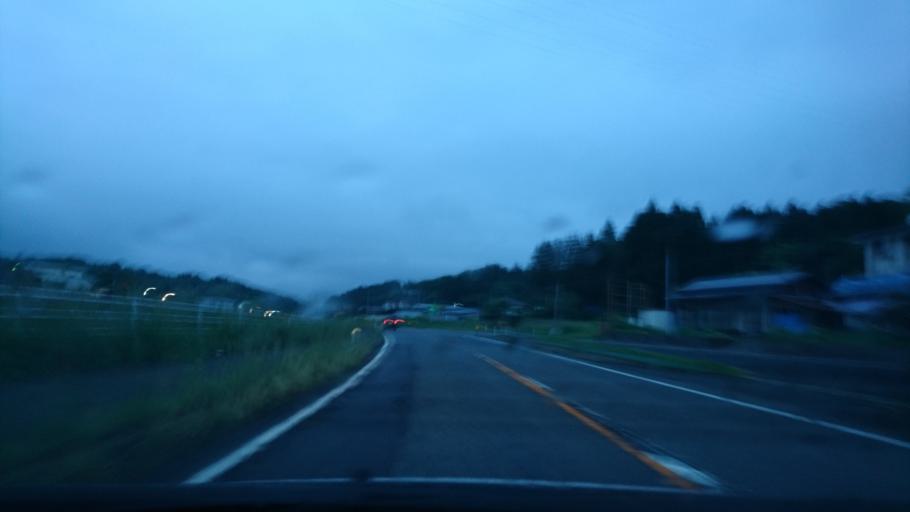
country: JP
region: Iwate
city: Ichinoseki
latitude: 38.7925
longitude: 141.0515
